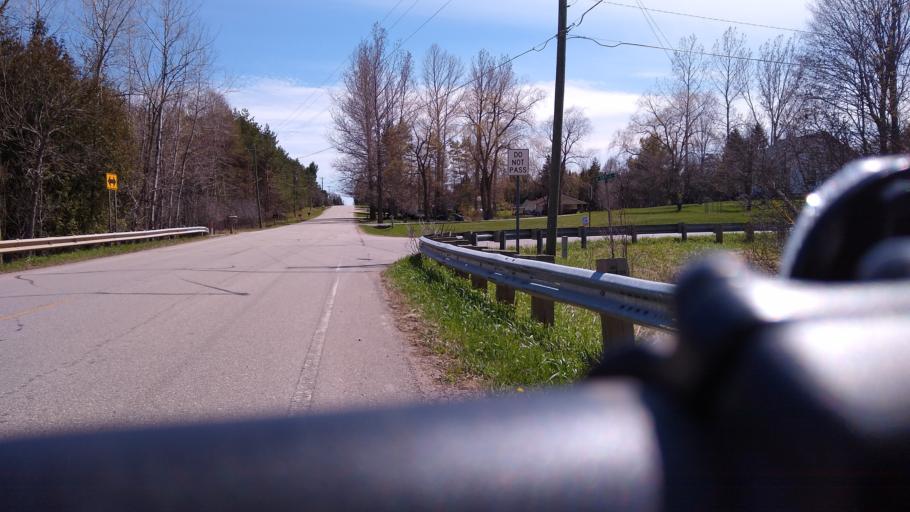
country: US
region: Michigan
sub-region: Delta County
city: Escanaba
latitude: 45.7246
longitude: -87.2025
